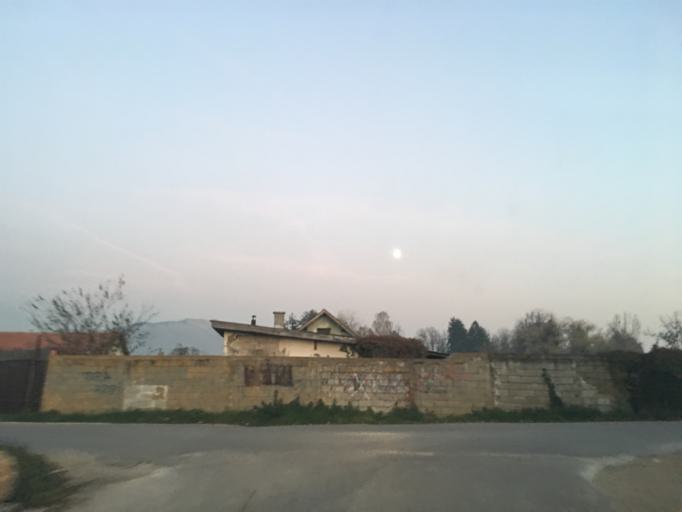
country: BA
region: Federation of Bosnia and Herzegovina
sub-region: Kanton Sarajevo
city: Sarajevo
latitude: 43.8163
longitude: 18.3465
